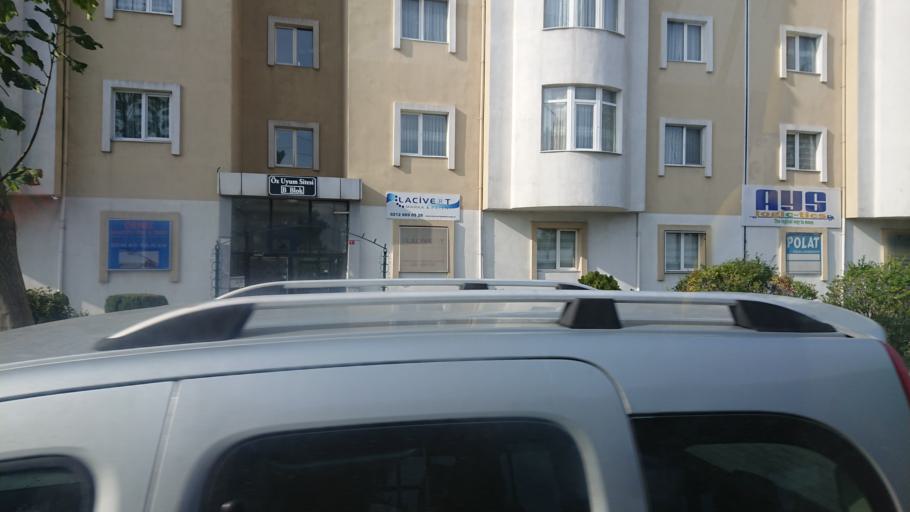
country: TR
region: Istanbul
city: Esenyurt
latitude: 41.0698
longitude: 28.6664
